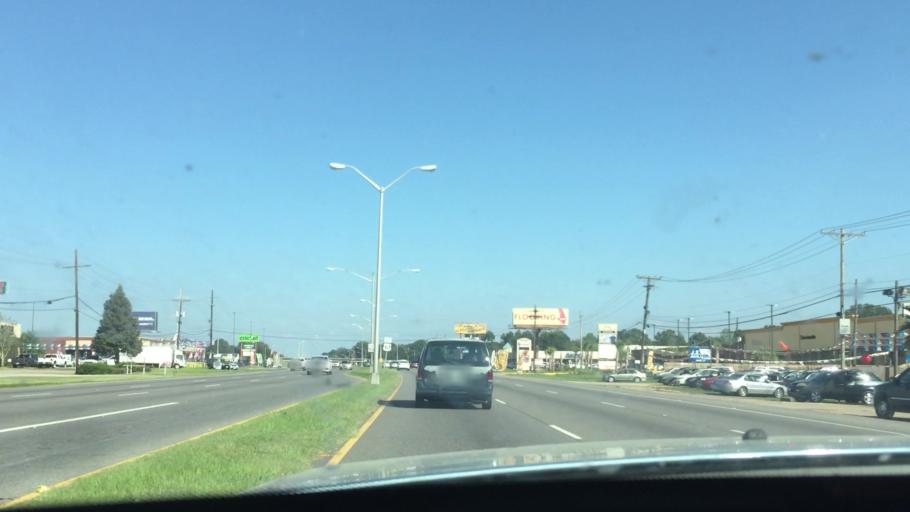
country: US
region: Louisiana
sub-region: East Baton Rouge Parish
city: Westminster
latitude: 30.4520
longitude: -91.1023
